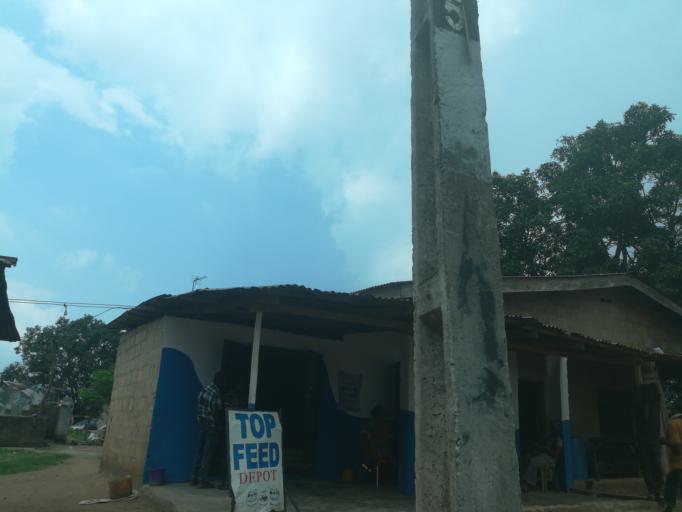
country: NG
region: Lagos
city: Ikorodu
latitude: 6.6710
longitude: 3.6699
